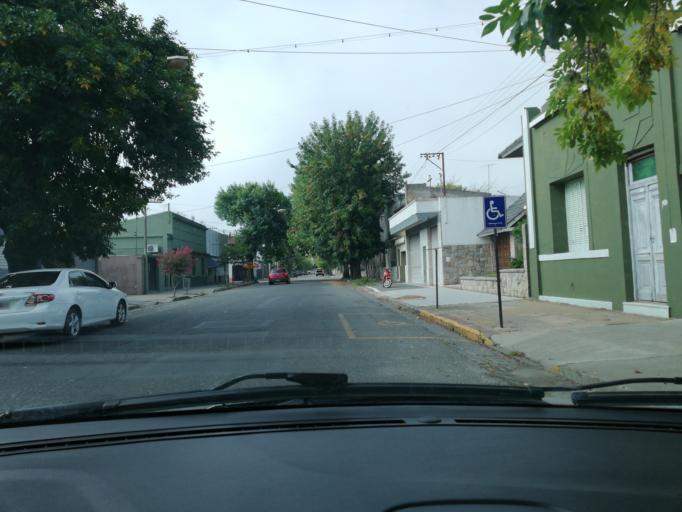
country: AR
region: Buenos Aires
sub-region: Partido de Balcarce
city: Balcarce
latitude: -37.8513
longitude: -58.2515
